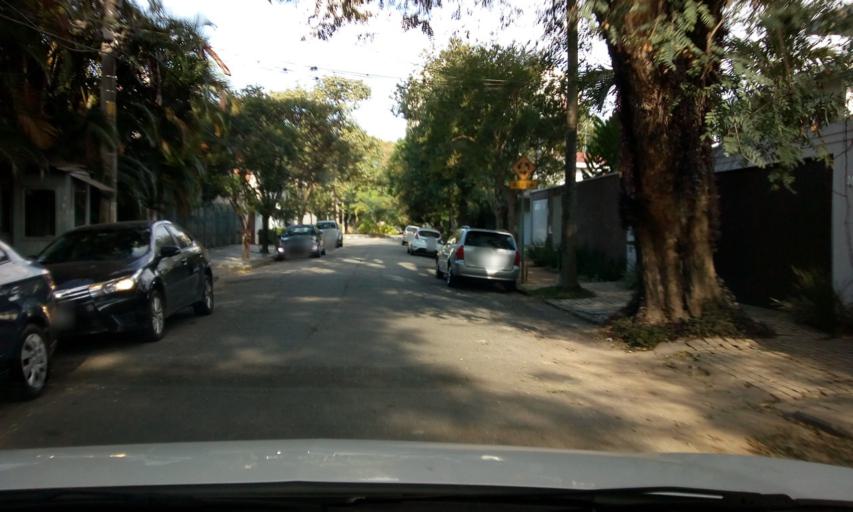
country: BR
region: Sao Paulo
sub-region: Sao Paulo
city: Sao Paulo
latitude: -23.5572
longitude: -46.7033
